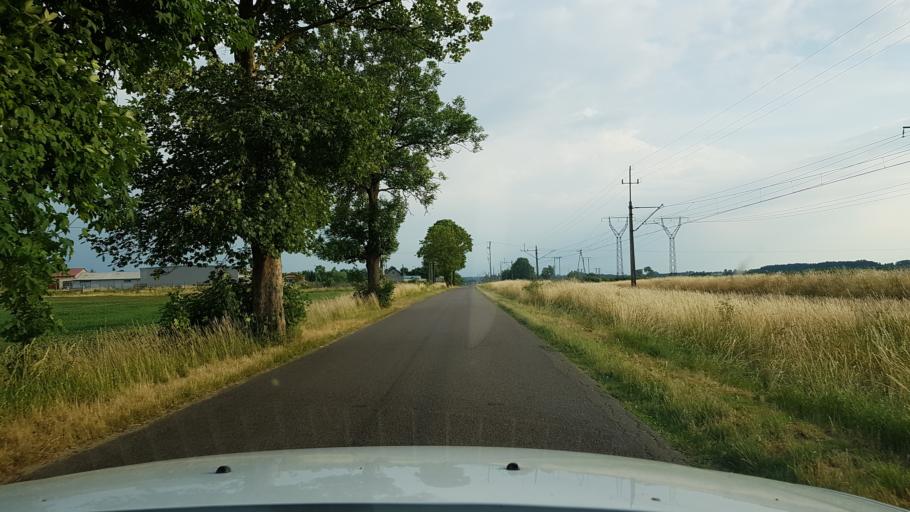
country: PL
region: West Pomeranian Voivodeship
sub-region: Powiat swidwinski
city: Swidwin
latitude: 53.7976
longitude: 15.7842
